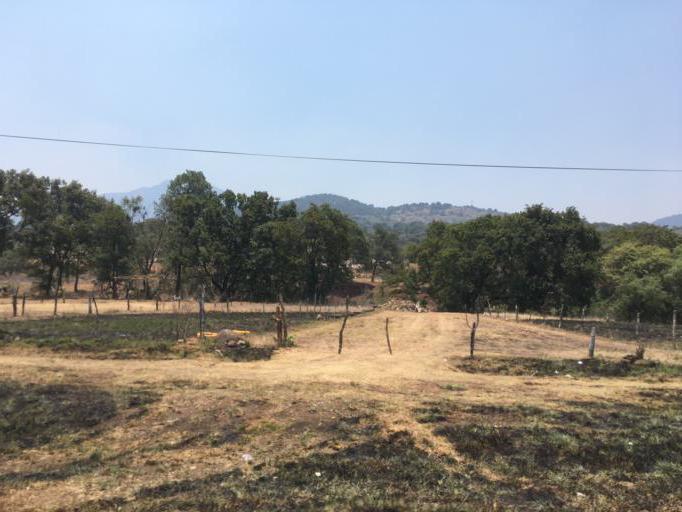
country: MX
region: Michoacan
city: Quiroga
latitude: 19.6571
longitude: -101.5061
